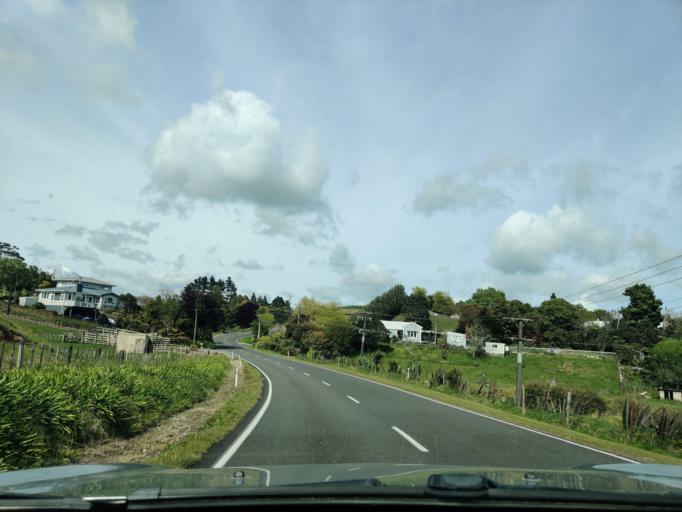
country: NZ
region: Taranaki
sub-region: New Plymouth District
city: New Plymouth
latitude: -39.0949
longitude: 174.1032
